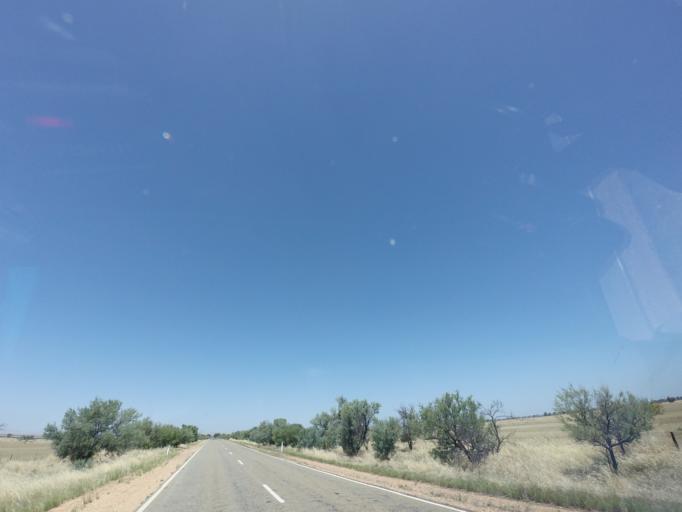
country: AU
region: South Australia
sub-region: Flinders Ranges
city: Quorn
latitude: -32.6663
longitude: 138.1676
